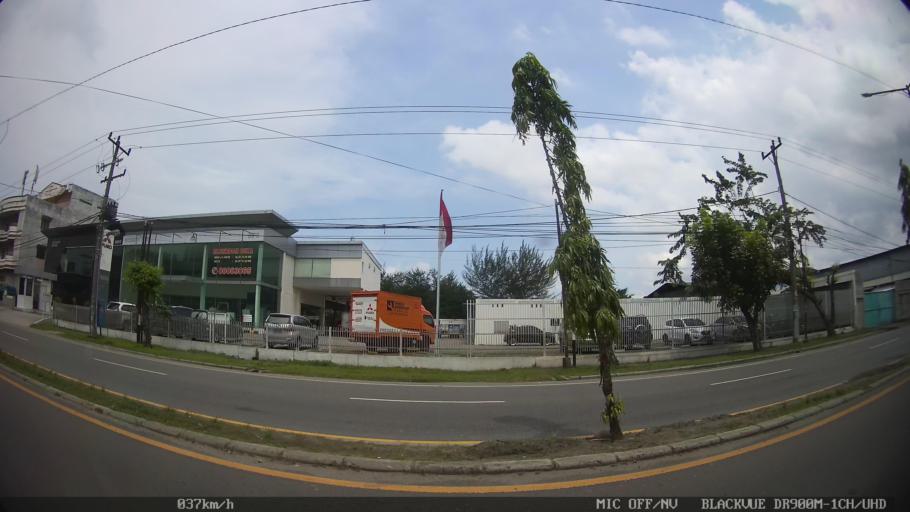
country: ID
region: North Sumatra
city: Medan
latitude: 3.6397
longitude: 98.6818
